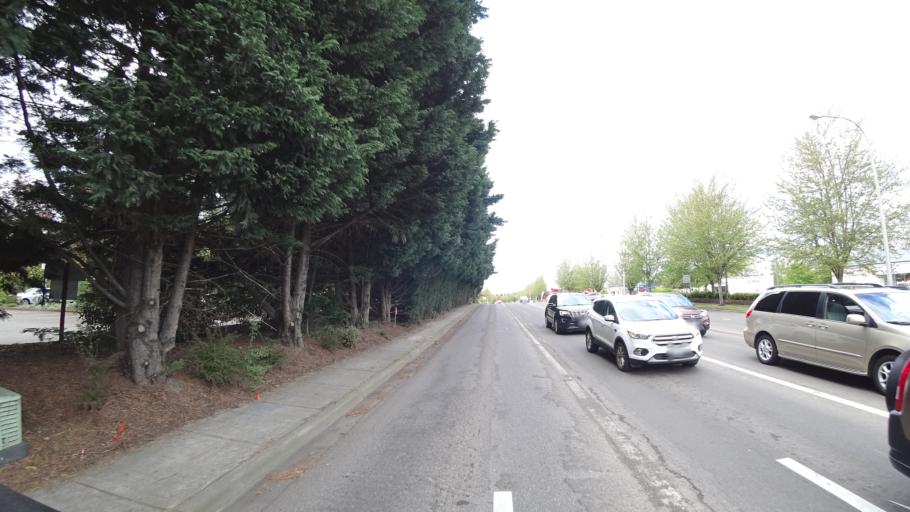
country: US
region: Oregon
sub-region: Washington County
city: Rockcreek
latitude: 45.5501
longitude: -122.9003
